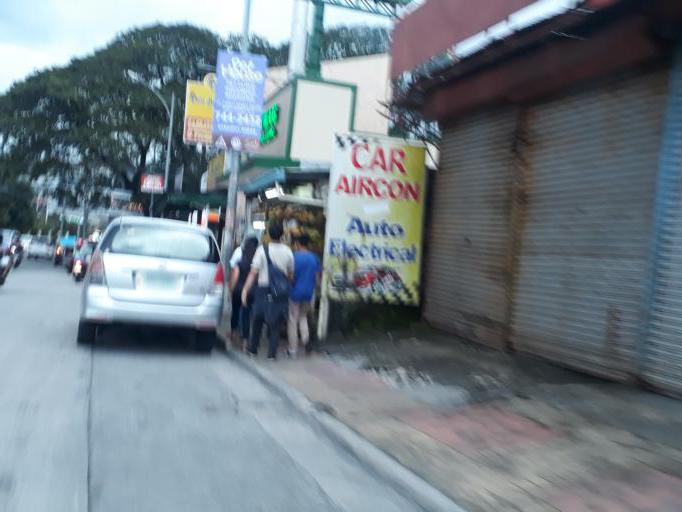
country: PH
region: Metro Manila
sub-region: Quezon City
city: Quezon City
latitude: 14.6836
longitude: 121.0786
